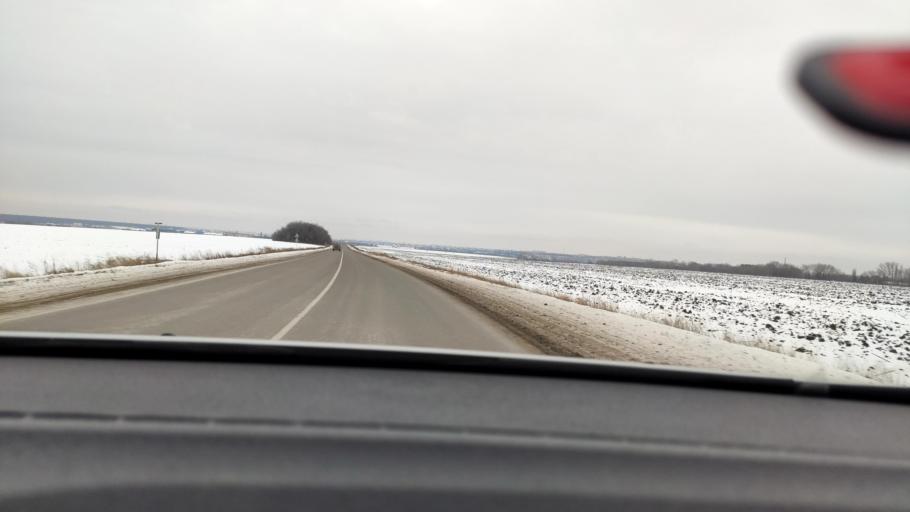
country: RU
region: Voronezj
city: Latnaya
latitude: 51.7356
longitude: 38.9493
